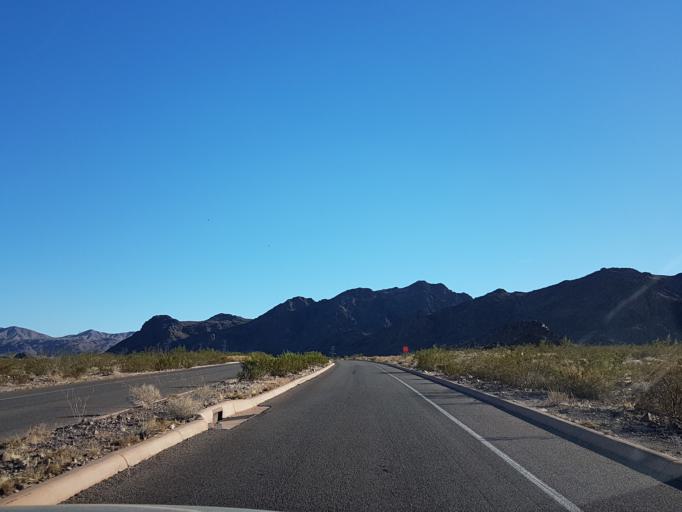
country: US
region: Nevada
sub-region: Clark County
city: Boulder City
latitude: 36.0554
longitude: -114.8198
